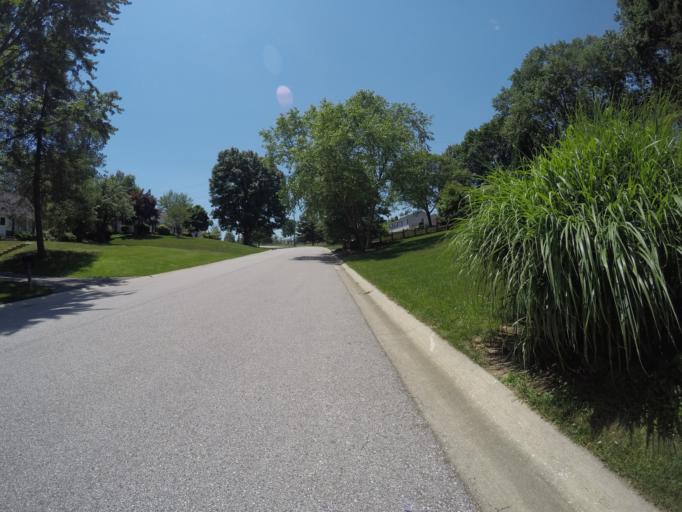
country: US
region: Maryland
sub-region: Howard County
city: Ilchester
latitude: 39.2374
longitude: -76.7868
